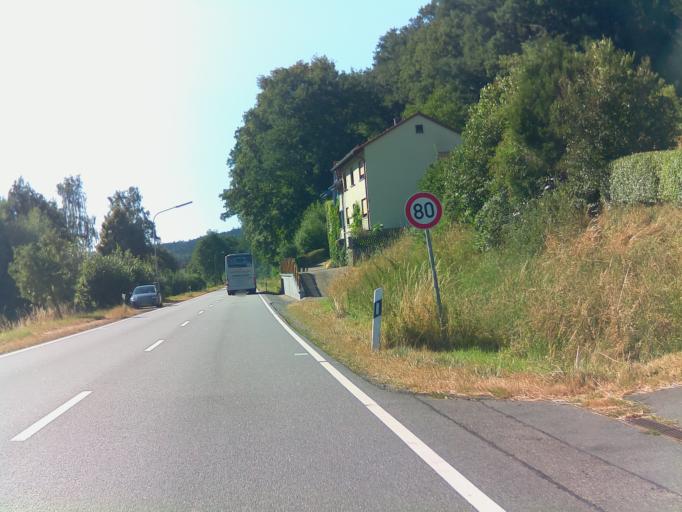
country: DE
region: Hesse
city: Reichelsheim
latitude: 49.6405
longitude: 8.8984
